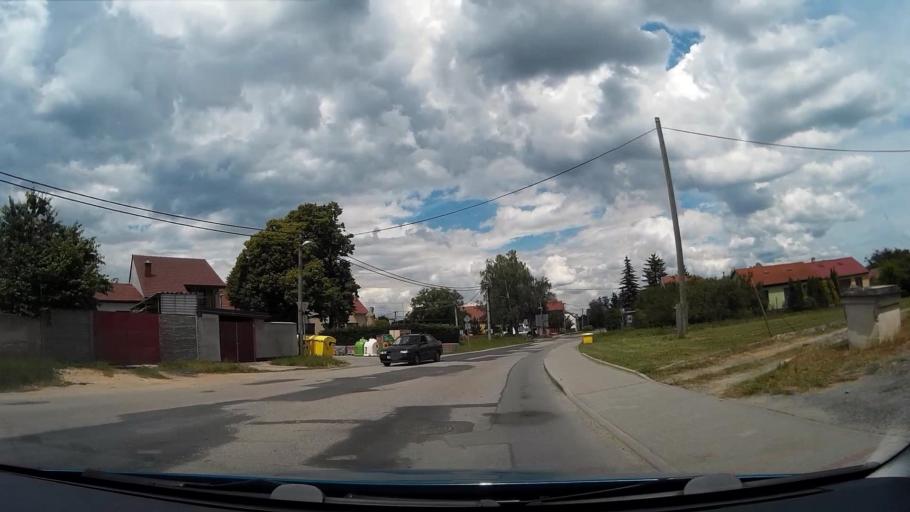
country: CZ
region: South Moravian
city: Orechov
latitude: 49.1169
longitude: 16.5257
